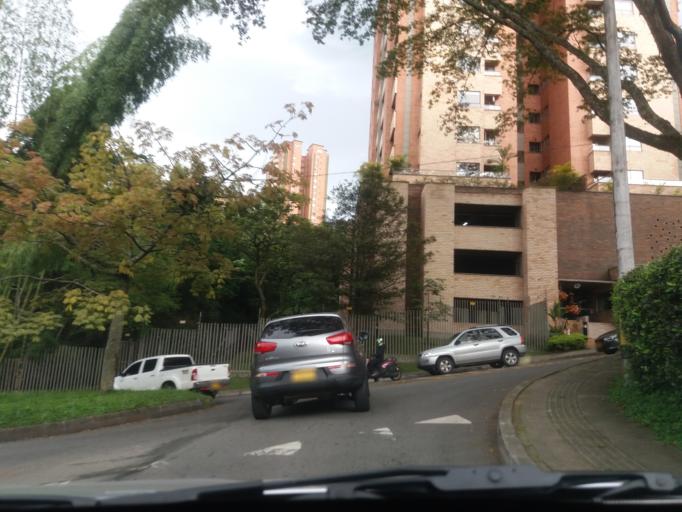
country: CO
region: Antioquia
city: Envigado
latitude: 6.1937
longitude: -75.5781
